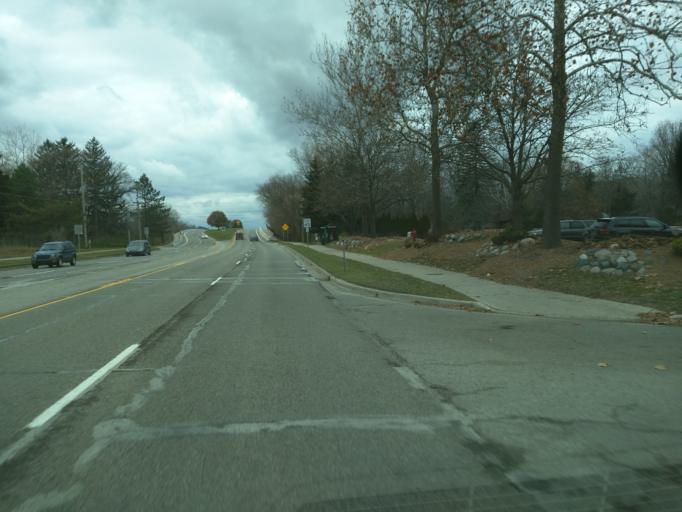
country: US
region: Michigan
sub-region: Ingham County
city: Okemos
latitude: 42.7244
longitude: -84.4410
